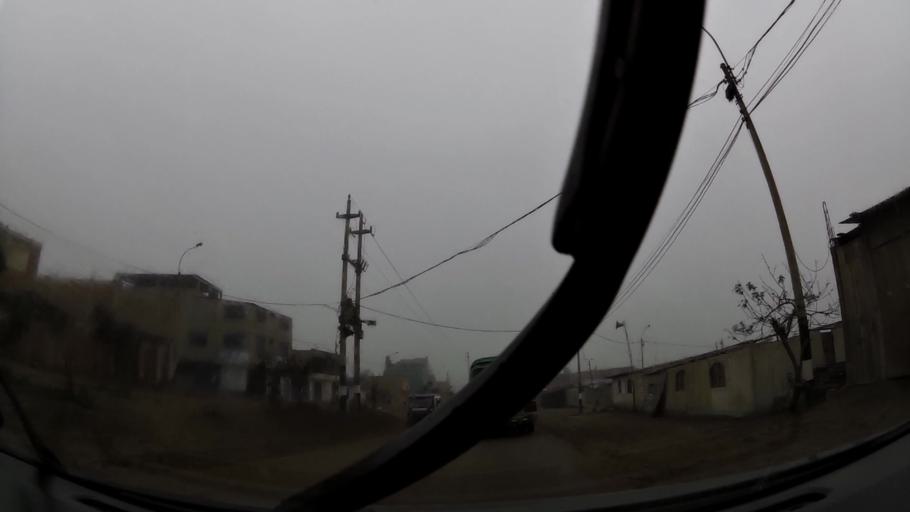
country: PE
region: Lima
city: Ventanilla
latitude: -11.8316
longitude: -77.1377
